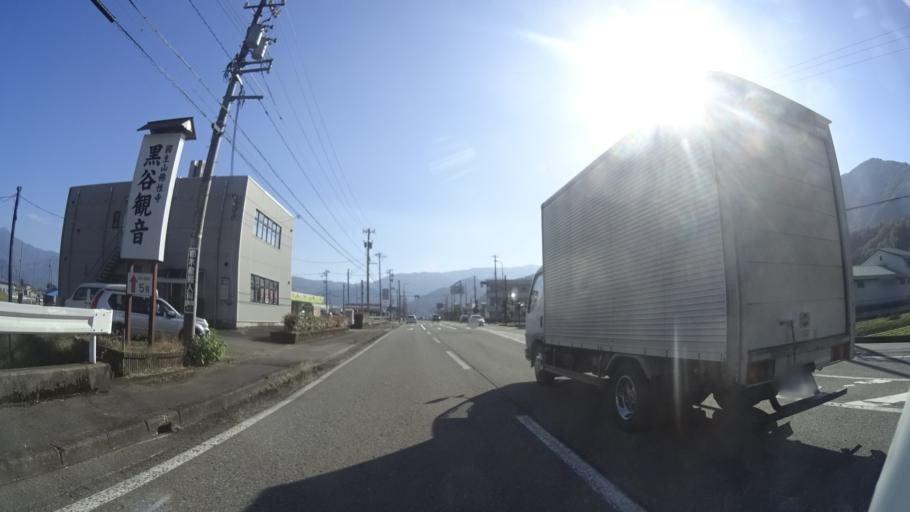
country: JP
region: Fukui
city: Ono
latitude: 35.9783
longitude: 136.4797
